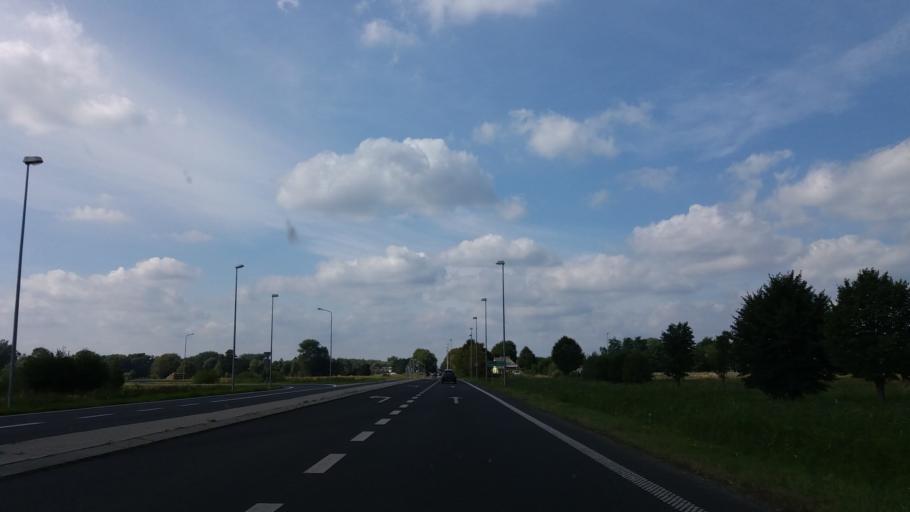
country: PL
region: West Pomeranian Voivodeship
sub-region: Powiat stargardzki
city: Kobylanka
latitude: 53.3487
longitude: 14.9482
